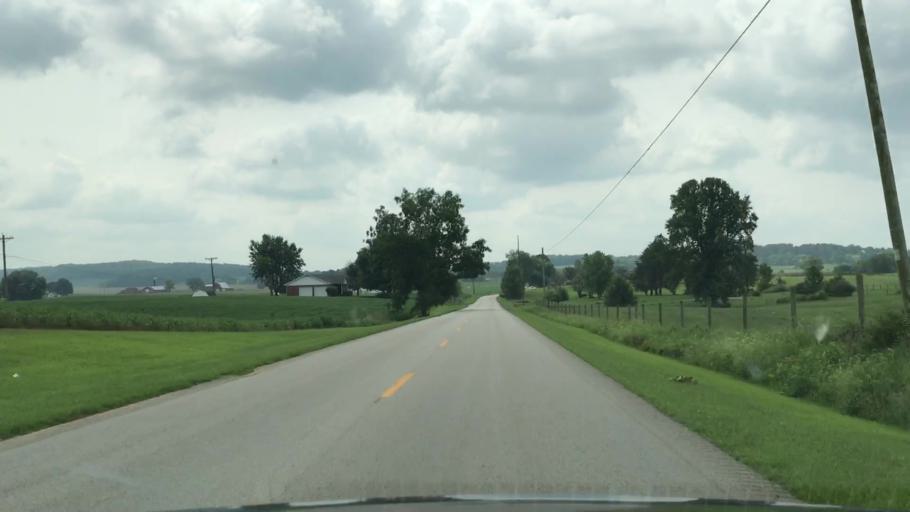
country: US
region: Kentucky
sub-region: Barren County
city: Cave City
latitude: 37.1018
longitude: -85.9774
